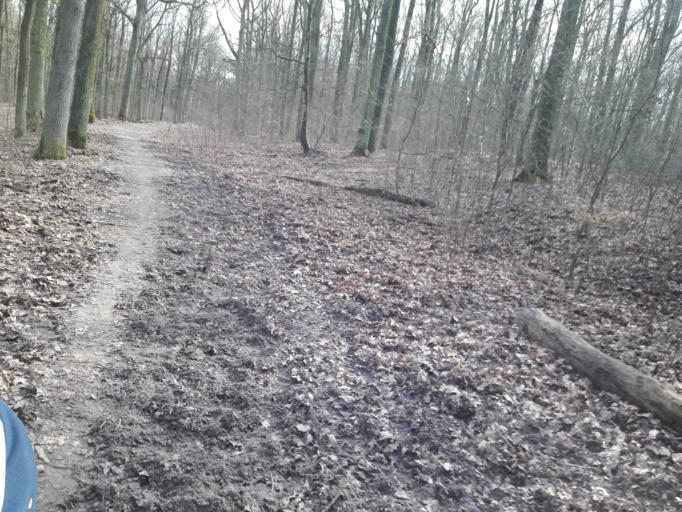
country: PL
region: Greater Poland Voivodeship
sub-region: Powiat poznanski
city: Suchy Las
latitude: 52.4816
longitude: 16.8951
